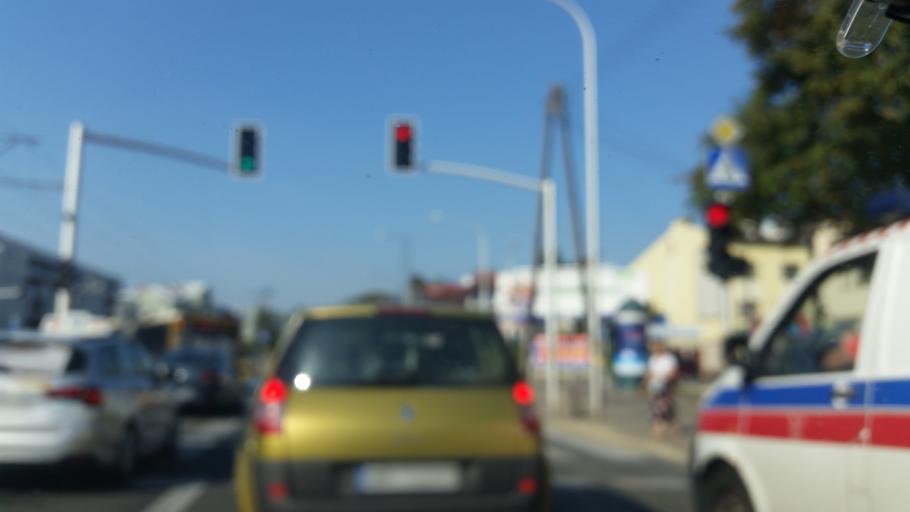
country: PL
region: Masovian Voivodeship
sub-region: Warszawa
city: Bemowo
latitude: 52.2287
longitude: 20.9156
